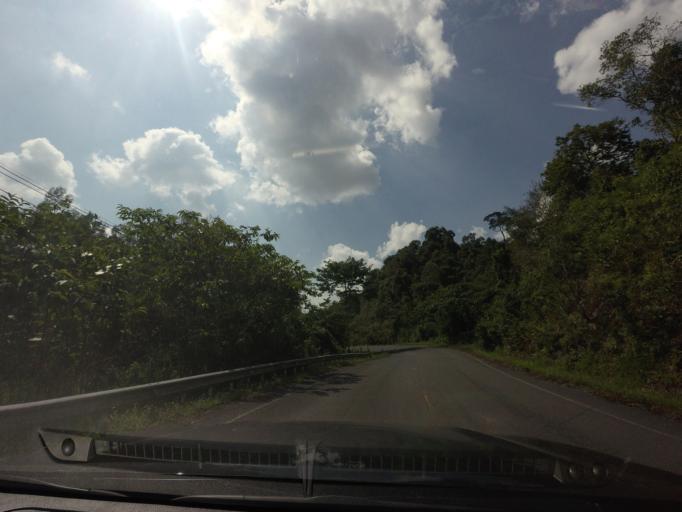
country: TH
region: Nan
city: Bo Kluea
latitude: 19.0763
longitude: 101.1393
